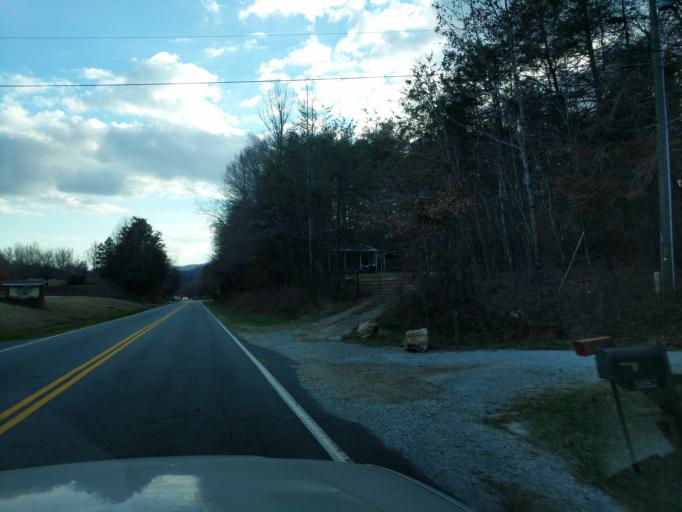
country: US
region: North Carolina
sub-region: McDowell County
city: West Marion
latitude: 35.6343
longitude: -81.9862
